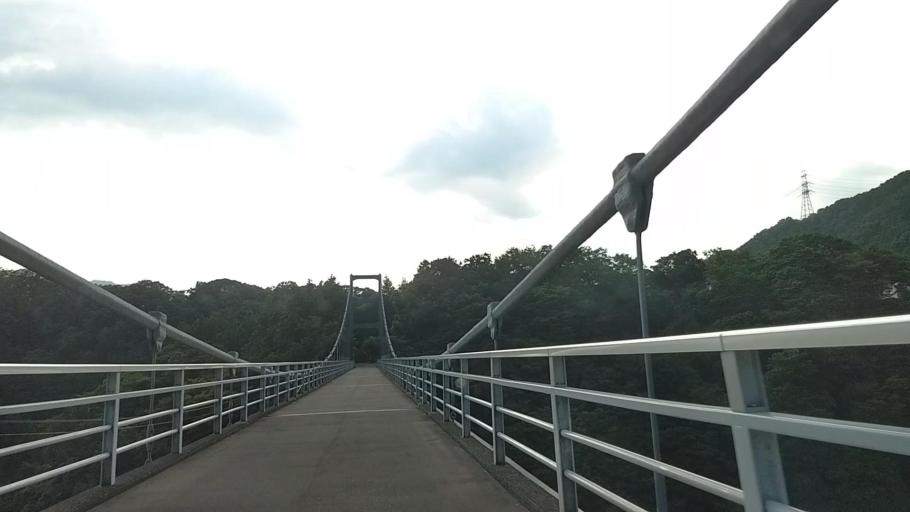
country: JP
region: Tokyo
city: Hachioji
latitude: 35.5983
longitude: 139.2429
